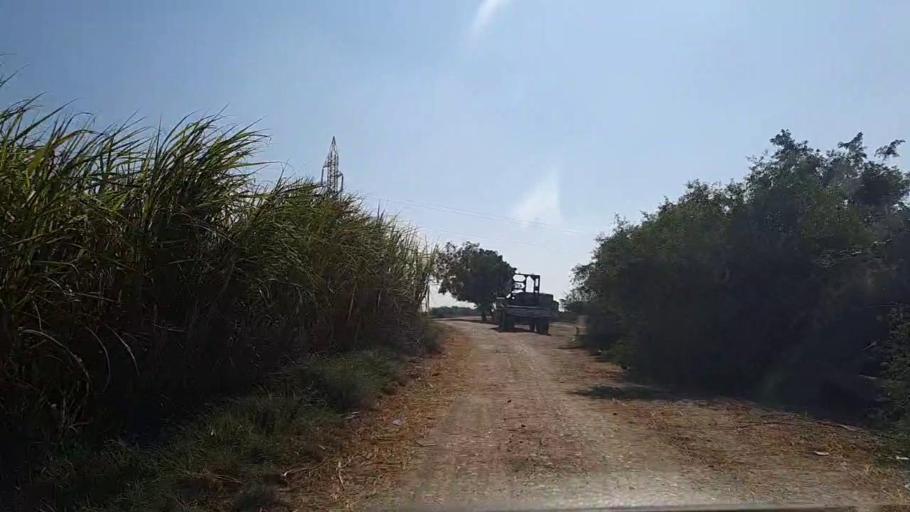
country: PK
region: Sindh
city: Mirpur Batoro
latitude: 24.6873
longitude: 68.1853
